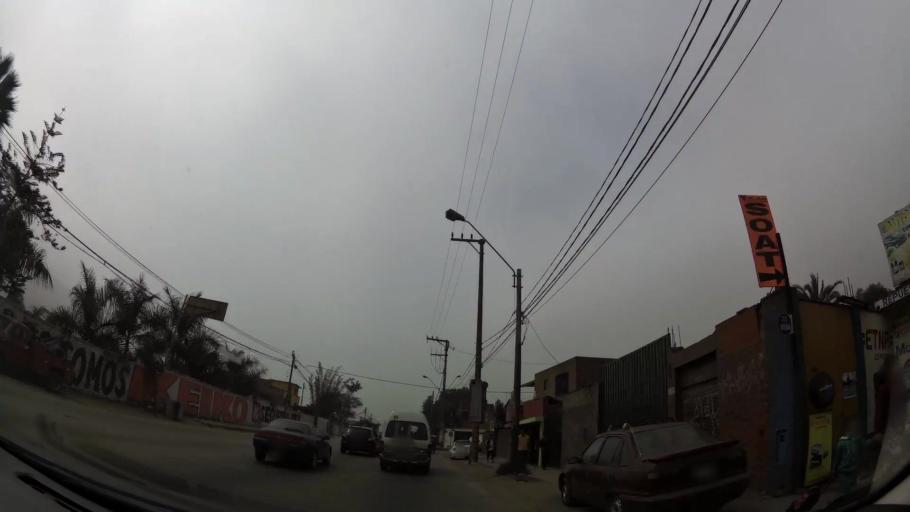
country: PE
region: Lima
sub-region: Lima
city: Chaclacayo
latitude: -11.9736
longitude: -76.7599
